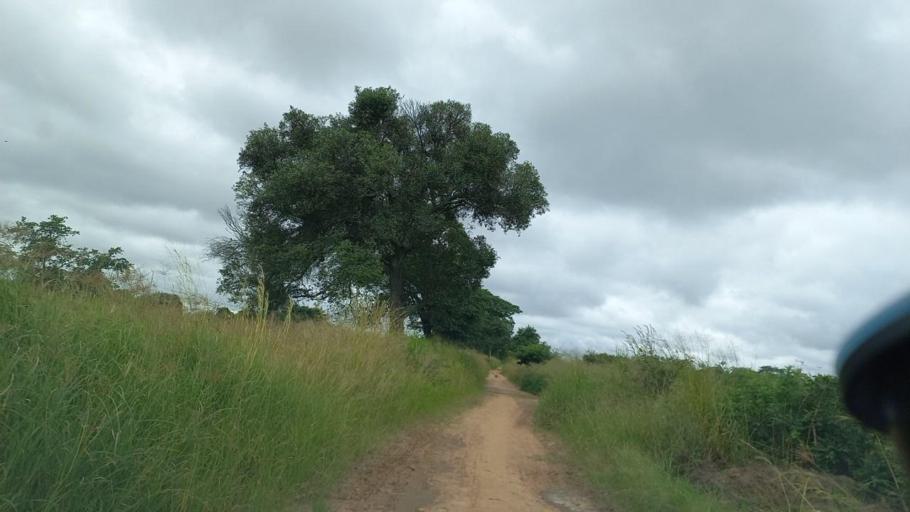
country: ZM
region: Lusaka
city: Lusaka
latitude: -15.1208
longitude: 28.3721
